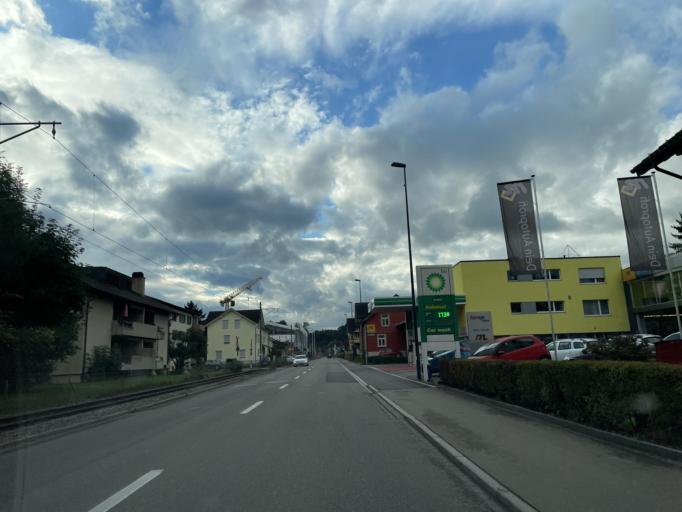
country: CH
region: Thurgau
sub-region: Muenchwilen District
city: Wangi
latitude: 47.4998
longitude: 8.9505
